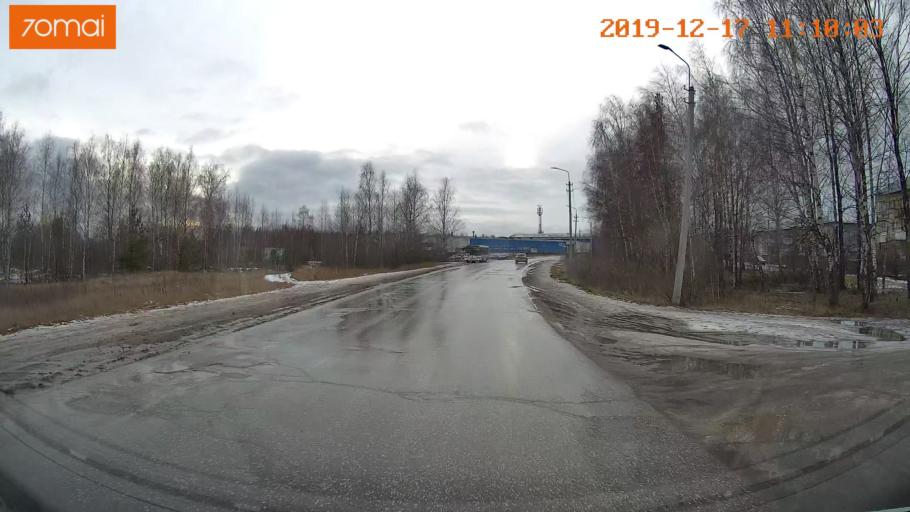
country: RU
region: Vladimir
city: Gus'-Khrustal'nyy
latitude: 55.5959
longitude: 40.6414
